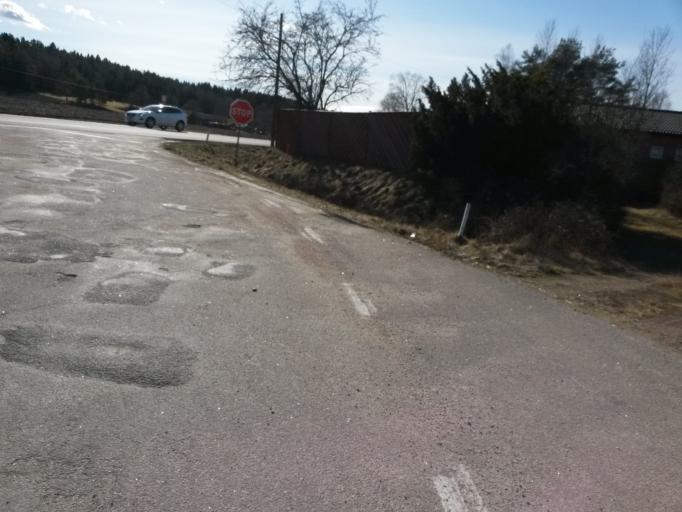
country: SE
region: Vaestra Goetaland
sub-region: Vargarda Kommun
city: Jonstorp
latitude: 57.9687
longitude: 12.6466
